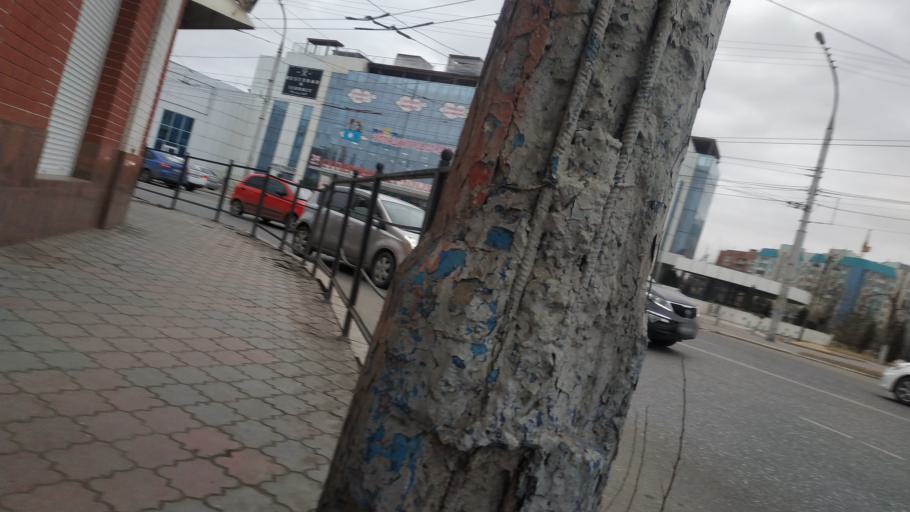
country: RU
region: Astrakhan
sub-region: Gorod Astrakhan'
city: Astrakhan'
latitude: 46.3429
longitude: 48.0206
